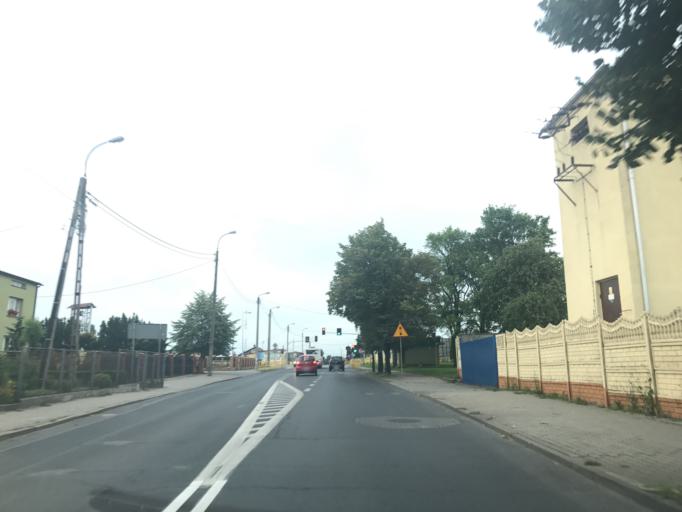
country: PL
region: Kujawsko-Pomorskie
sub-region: Powiat lipnowski
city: Lipno
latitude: 52.8516
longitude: 19.1755
